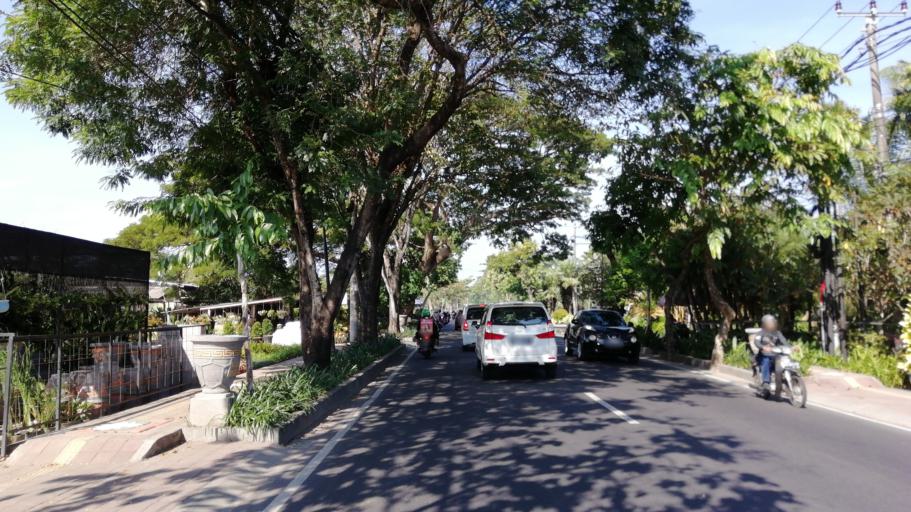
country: ID
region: Bali
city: Banjar Batanpoh
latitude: -8.6737
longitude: 115.2482
